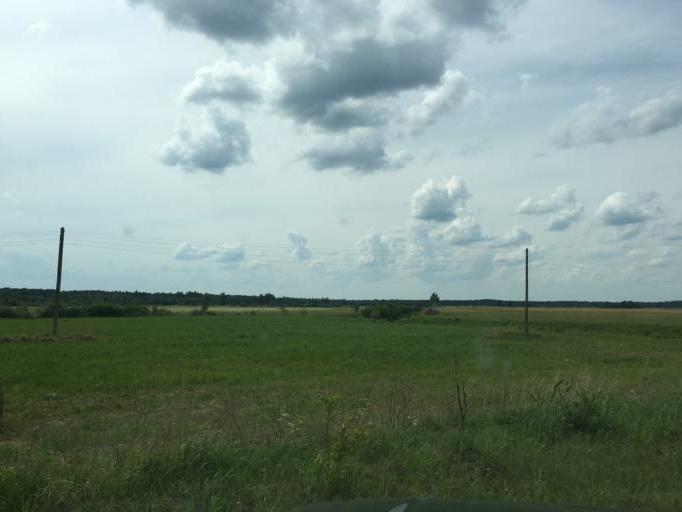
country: LV
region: Rugaju
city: Rugaji
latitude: 56.9794
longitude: 27.0495
